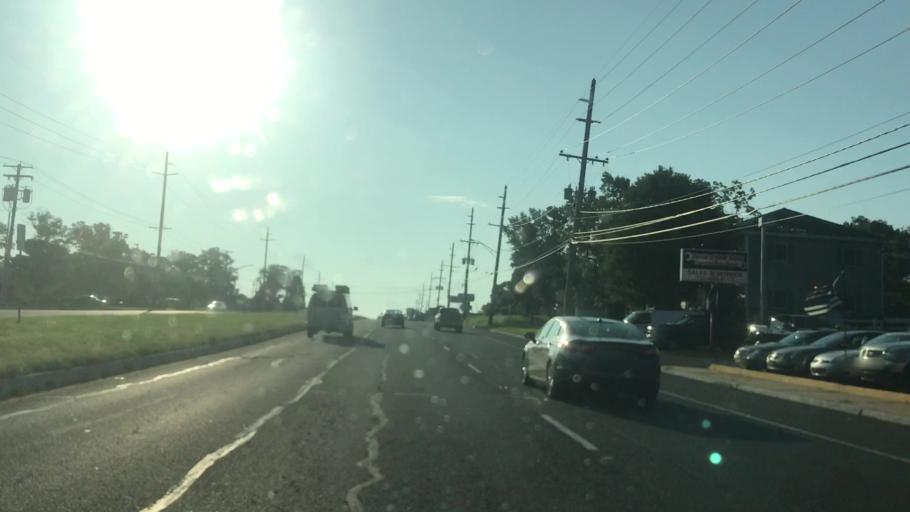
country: US
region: New Jersey
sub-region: Ocean County
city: Island Heights
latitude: 39.9540
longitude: -74.1517
